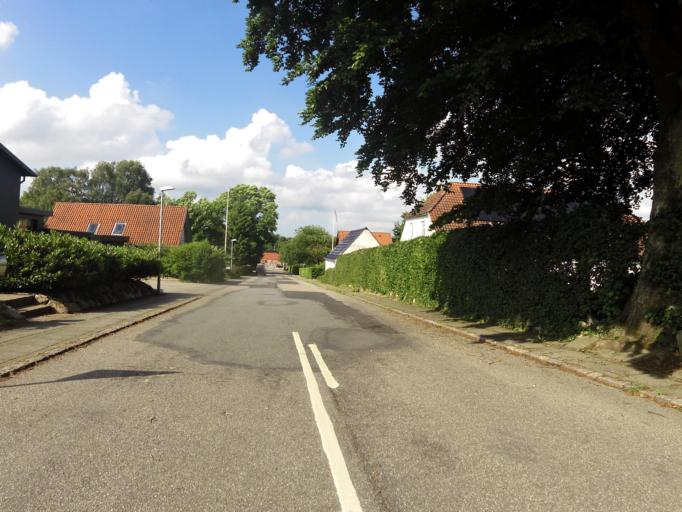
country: DK
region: South Denmark
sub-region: Vejen Kommune
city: Rodding
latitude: 55.3656
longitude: 9.0603
